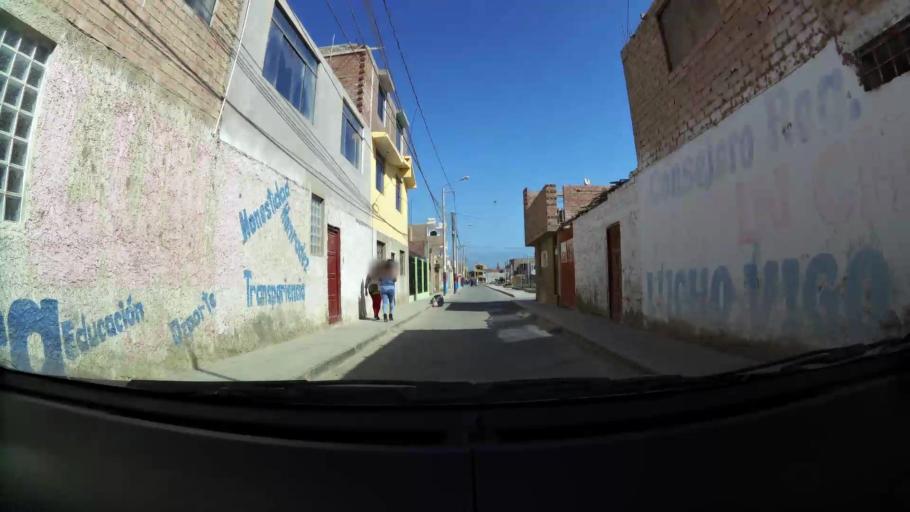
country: PE
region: Ancash
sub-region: Provincia de Huarmey
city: Huarmey
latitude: -10.0691
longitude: -78.1491
